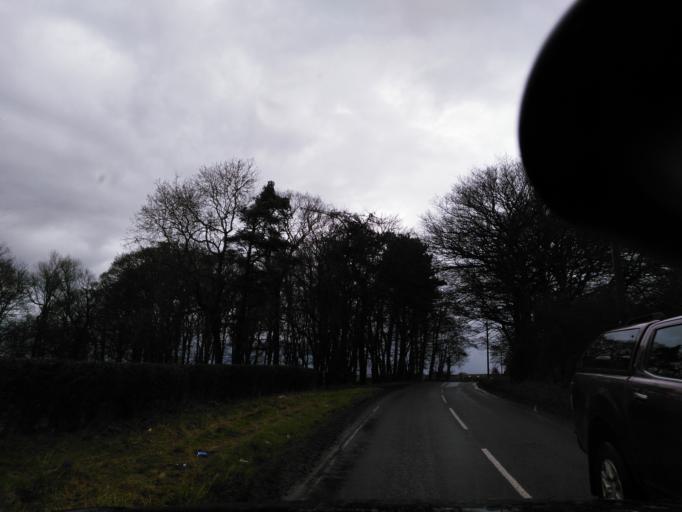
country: GB
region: England
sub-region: North Yorkshire
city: Ripon
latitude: 54.1445
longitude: -1.4530
